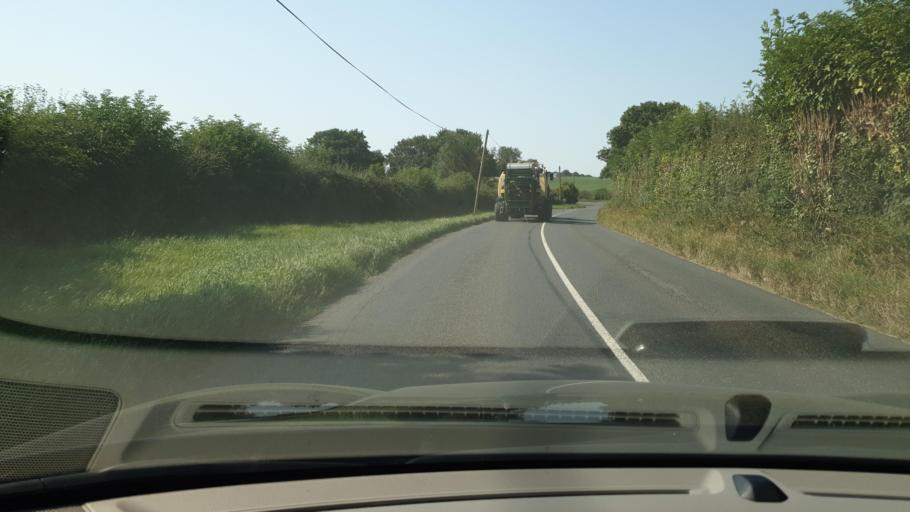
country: IE
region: Leinster
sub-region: An Mhi
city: Athboy
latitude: 53.5911
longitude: -6.8599
